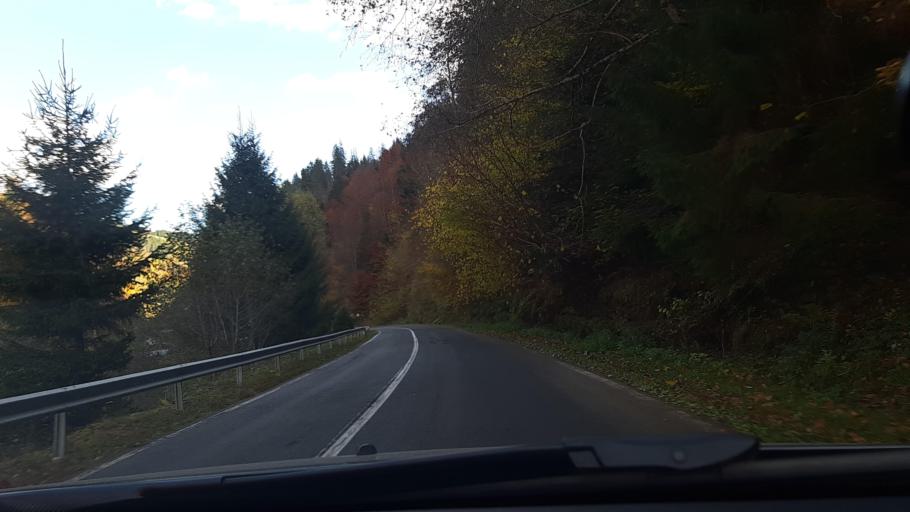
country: RO
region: Valcea
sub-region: Comuna Voineasa
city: Voineasa
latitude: 45.4242
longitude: 23.9417
